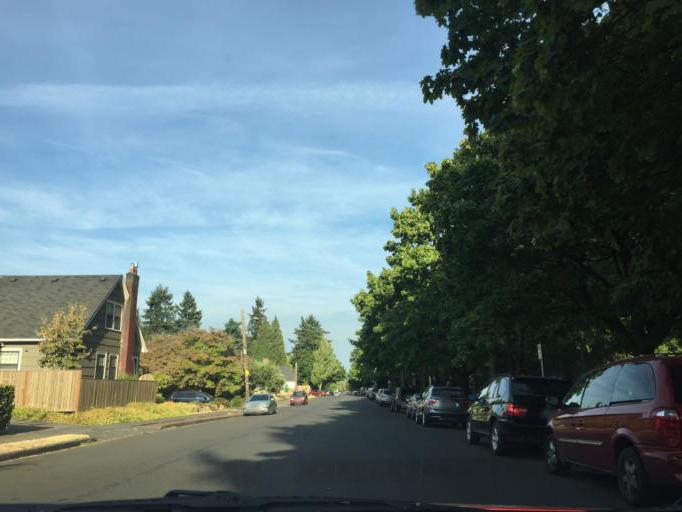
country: US
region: Oregon
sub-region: Multnomah County
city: Portland
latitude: 45.5537
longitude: -122.6305
